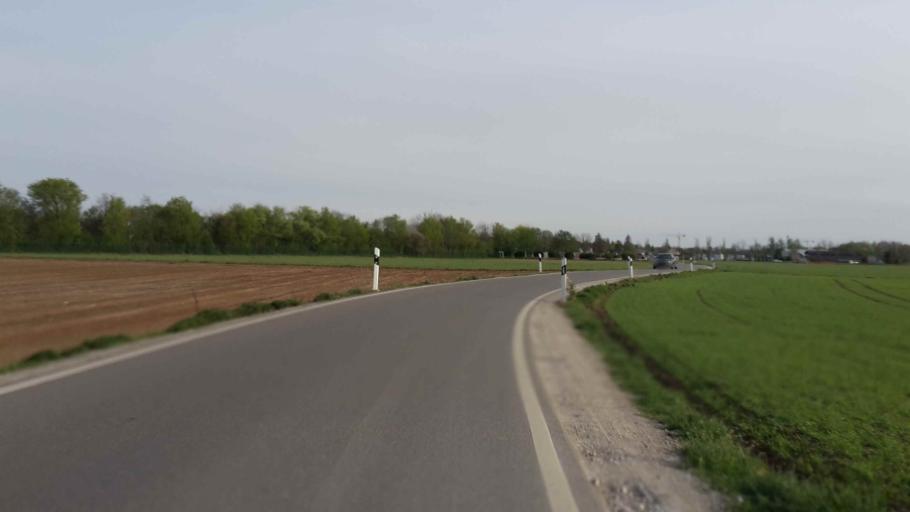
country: DE
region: Bavaria
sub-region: Upper Bavaria
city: Pasing
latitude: 48.1785
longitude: 11.4537
